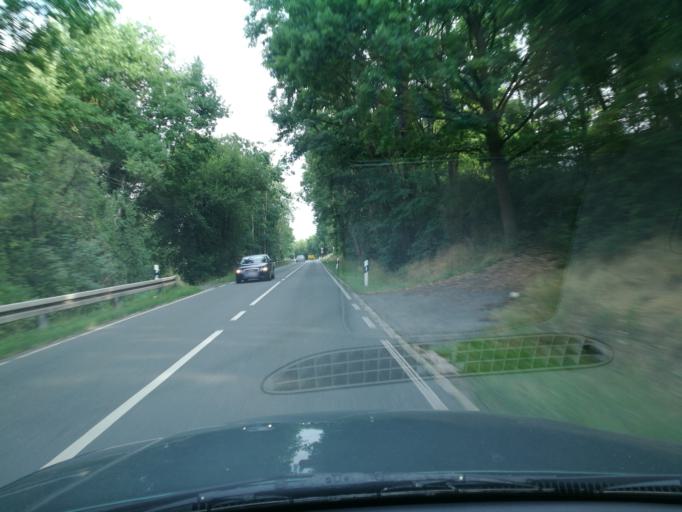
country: DE
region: Bavaria
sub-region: Regierungsbezirk Mittelfranken
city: Obermichelbach
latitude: 49.5285
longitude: 10.9482
